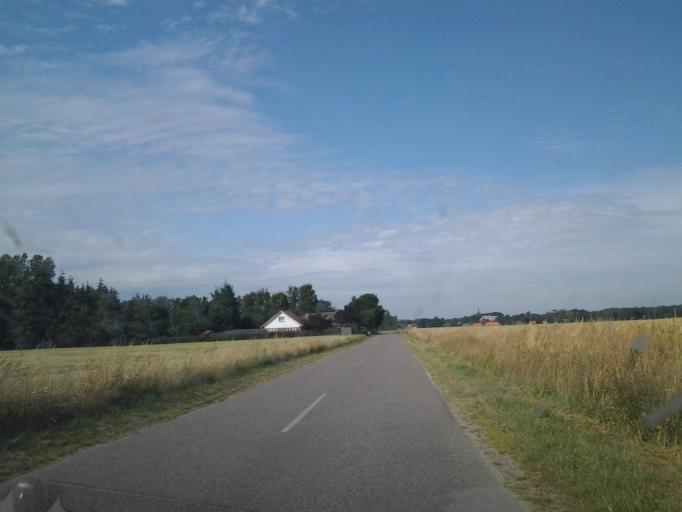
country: DE
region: Schleswig-Holstein
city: Aventoft
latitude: 54.9284
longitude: 8.7982
